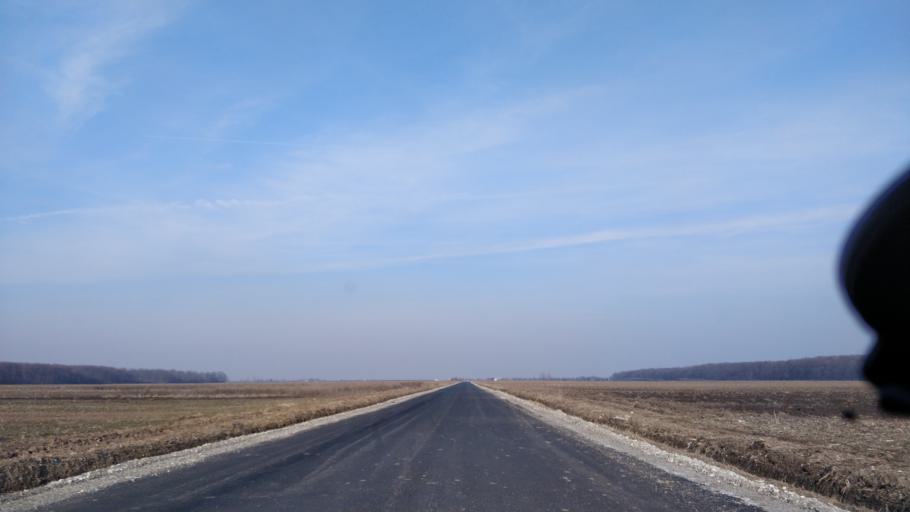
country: RO
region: Giurgiu
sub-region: Comuna Ulmi
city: Trestieni
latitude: 44.5241
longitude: 25.7807
